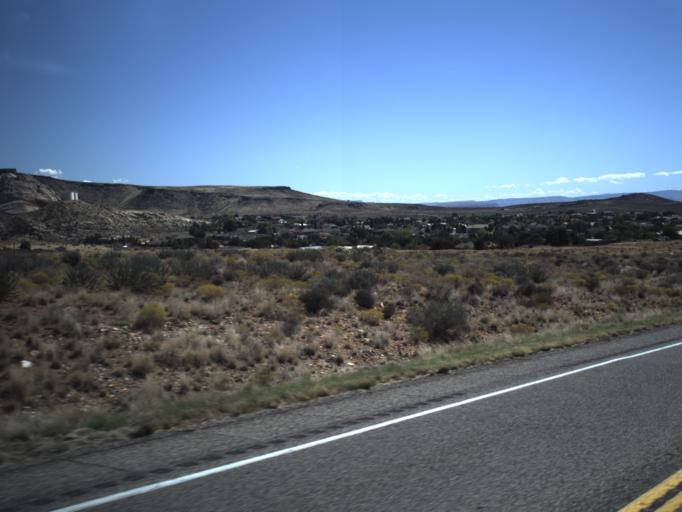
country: US
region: Utah
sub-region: Washington County
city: Ivins
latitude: 37.2150
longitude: -113.6324
